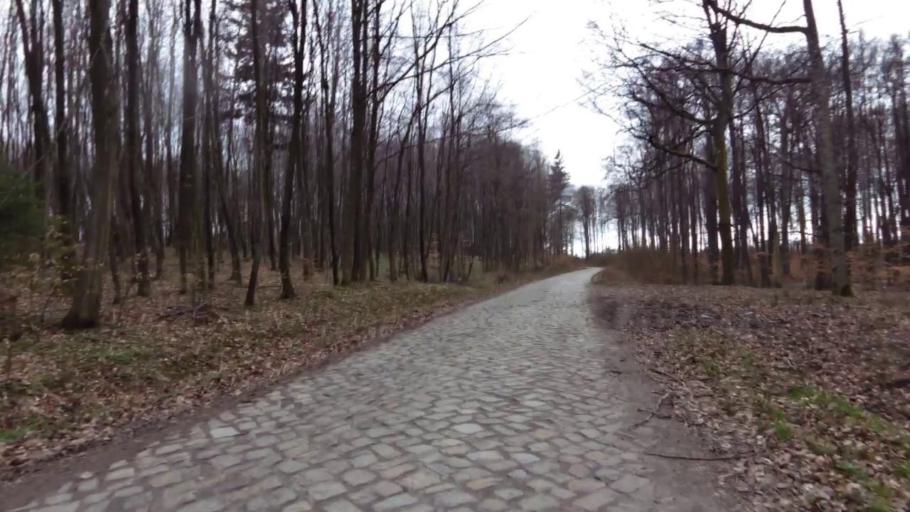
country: PL
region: West Pomeranian Voivodeship
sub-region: Powiat koszalinski
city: Sianow
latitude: 54.2710
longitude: 16.3195
